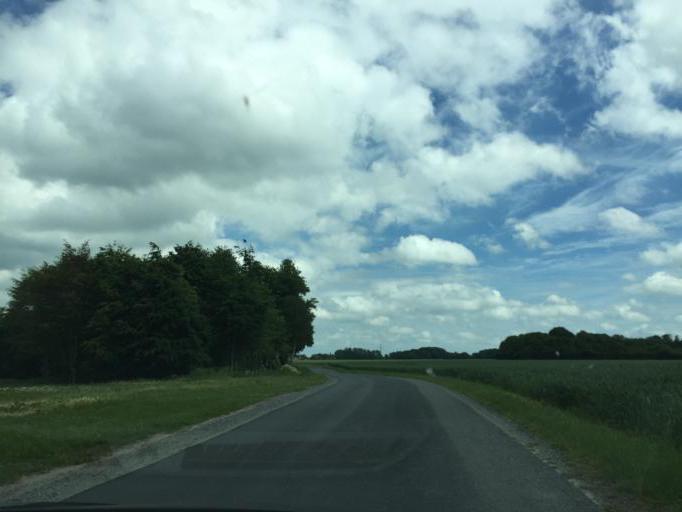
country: DK
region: South Denmark
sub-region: Faaborg-Midtfyn Kommune
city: Ringe
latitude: 55.2537
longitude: 10.4290
